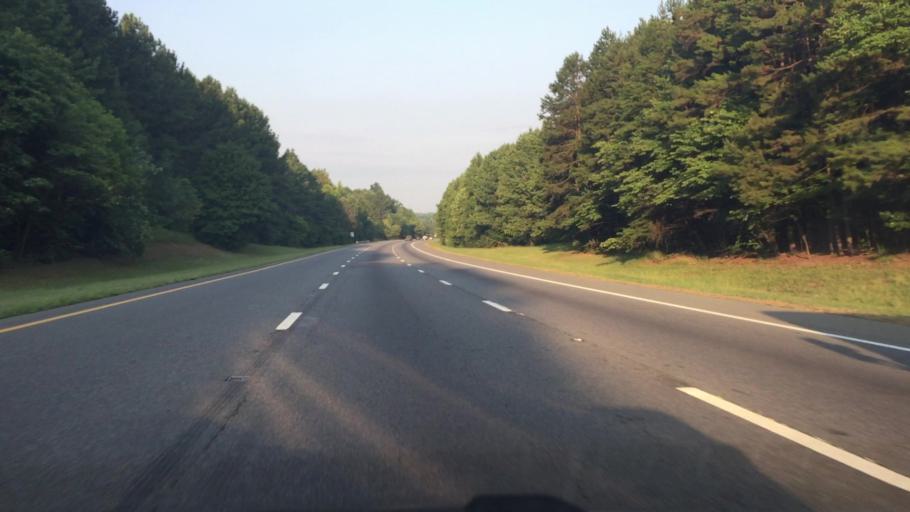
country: US
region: North Carolina
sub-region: Davidson County
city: Lexington
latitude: 35.7907
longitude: -80.2260
